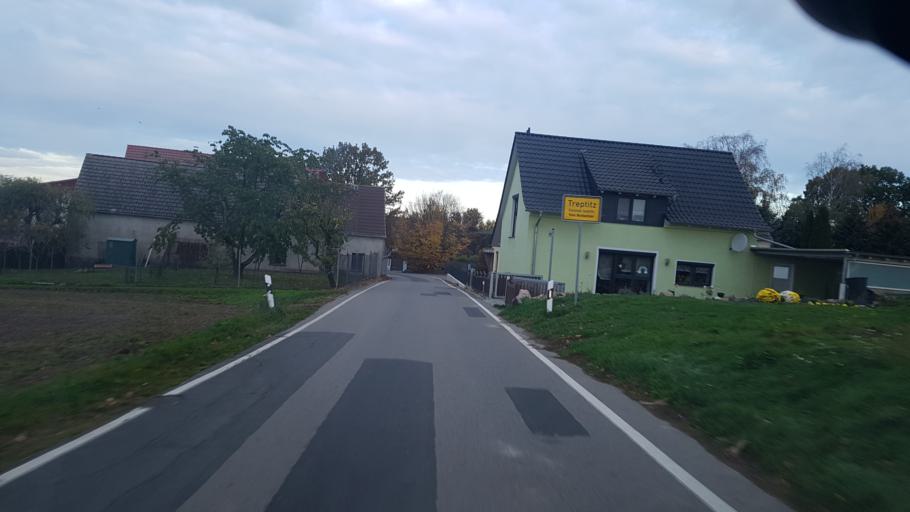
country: DE
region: Saxony
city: Cavertitz
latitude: 51.4005
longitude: 13.1344
